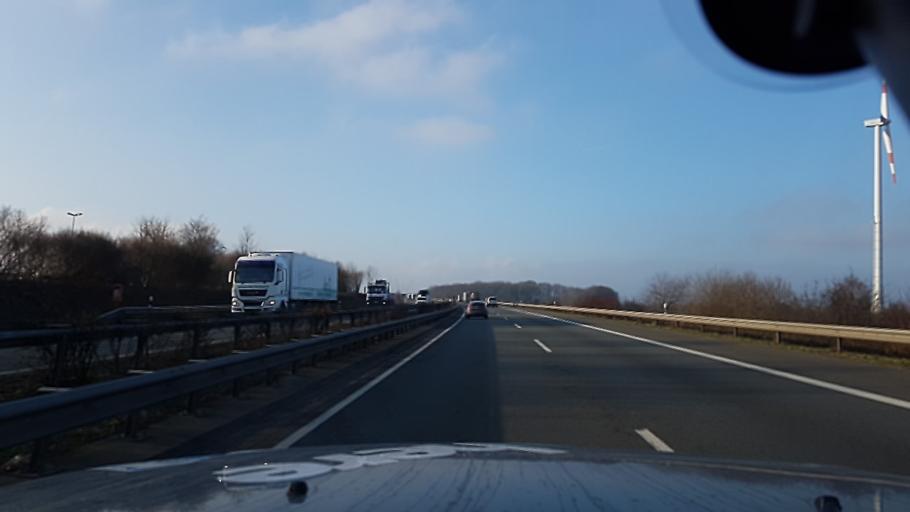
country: DE
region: Lower Saxony
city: Salzbergen
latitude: 52.3419
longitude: 7.3993
